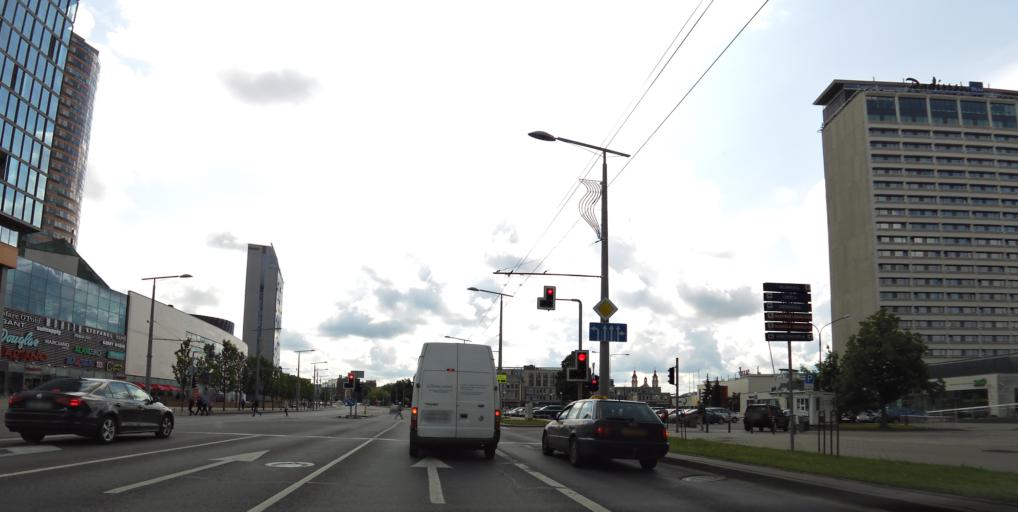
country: LT
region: Vilnius County
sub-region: Vilnius
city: Vilnius
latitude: 54.6963
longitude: 25.2746
